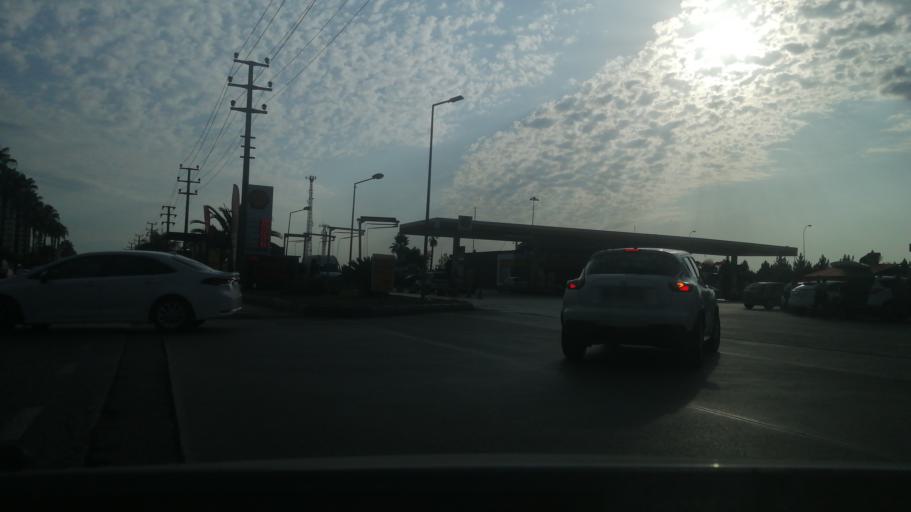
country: TR
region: Adana
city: Seyhan
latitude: 37.0299
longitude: 35.2550
